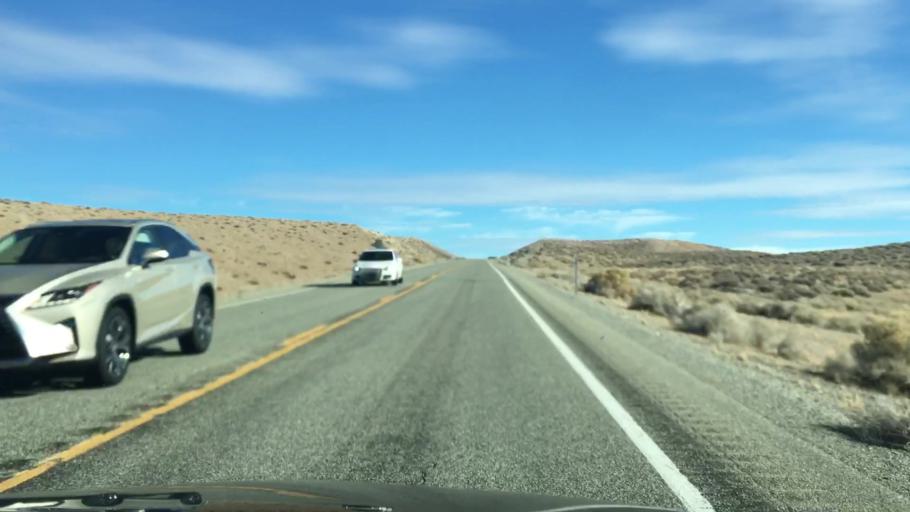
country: US
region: Nevada
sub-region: Lyon County
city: Yerington
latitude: 39.0453
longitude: -118.9619
